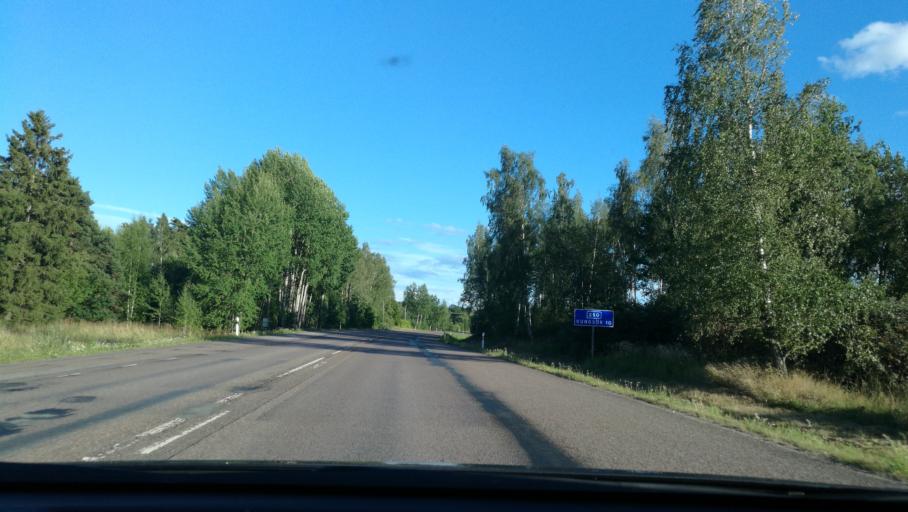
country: SE
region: Vaestmanland
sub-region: Kopings Kommun
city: Koping
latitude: 59.4814
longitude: 15.9862
